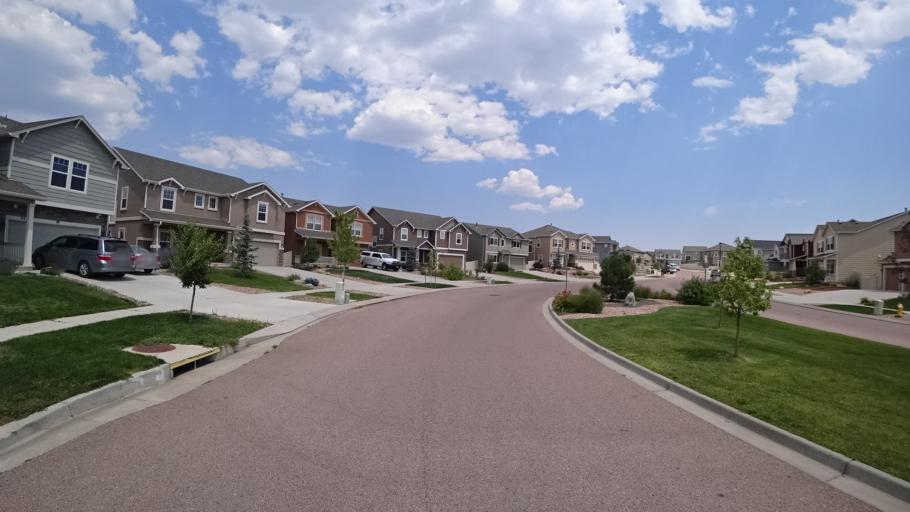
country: US
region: Colorado
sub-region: El Paso County
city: Black Forest
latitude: 38.9506
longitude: -104.6957
